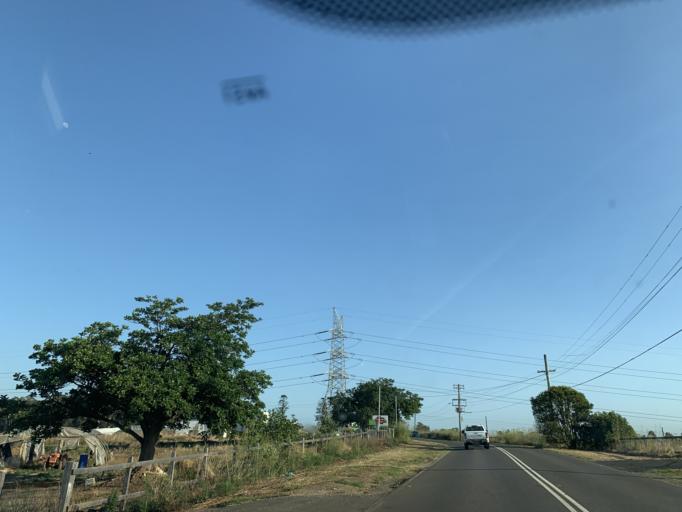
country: AU
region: New South Wales
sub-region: Fairfield
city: Horsley Park
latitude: -33.8377
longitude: 150.8794
